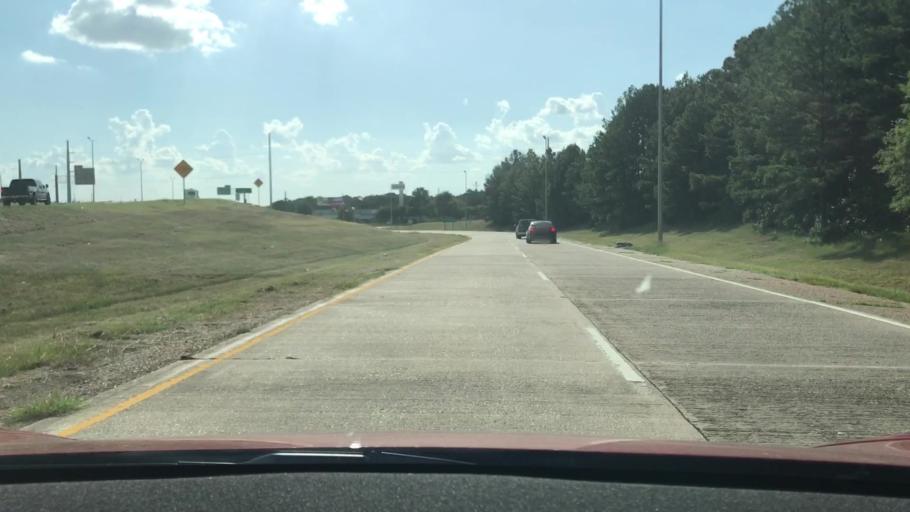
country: US
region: Louisiana
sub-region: Bossier Parish
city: Bossier City
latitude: 32.4208
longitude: -93.7600
